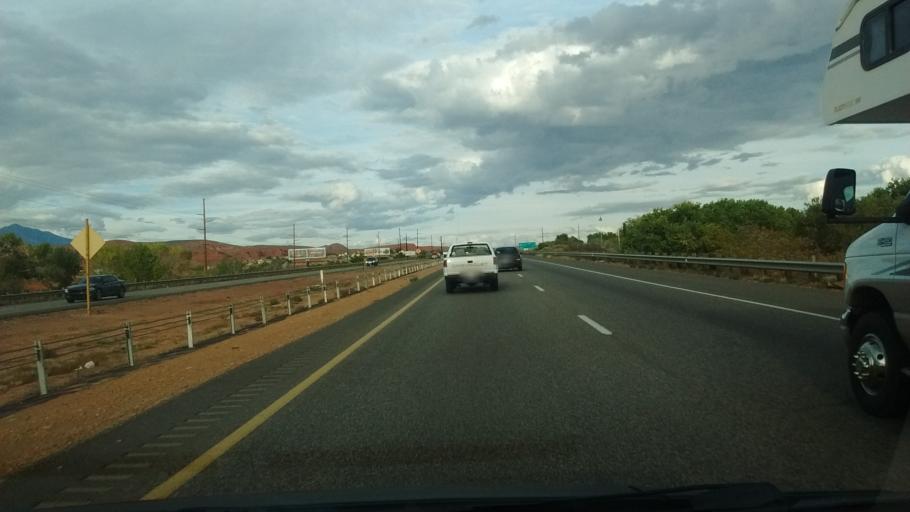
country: US
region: Utah
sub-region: Washington County
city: Washington
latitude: 37.1358
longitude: -113.5143
